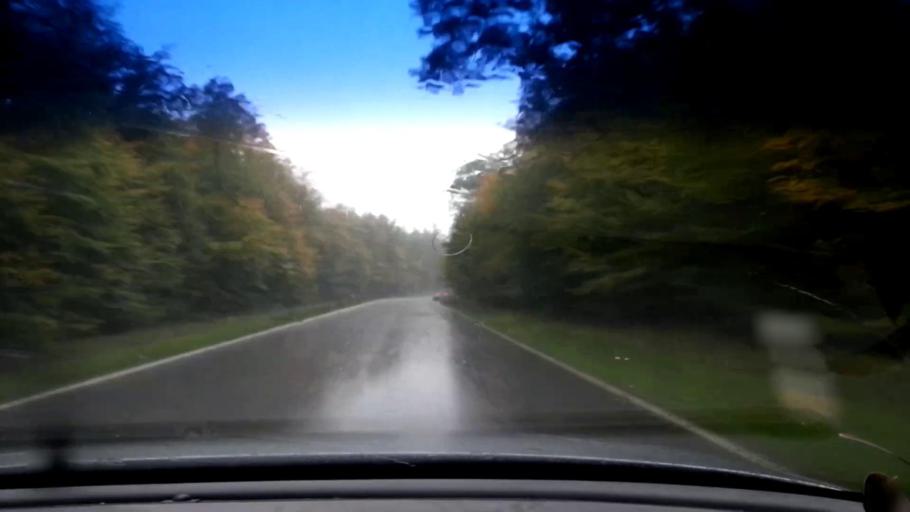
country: DE
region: Bavaria
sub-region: Upper Franconia
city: Litzendorf
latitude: 49.9302
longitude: 10.9976
